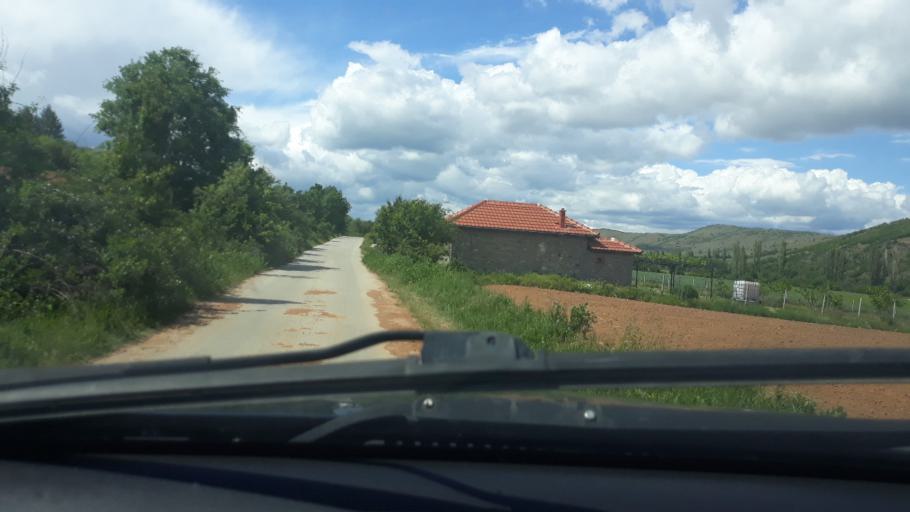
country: MK
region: Krivogastani
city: Krivogashtani
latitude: 41.3502
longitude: 21.2979
